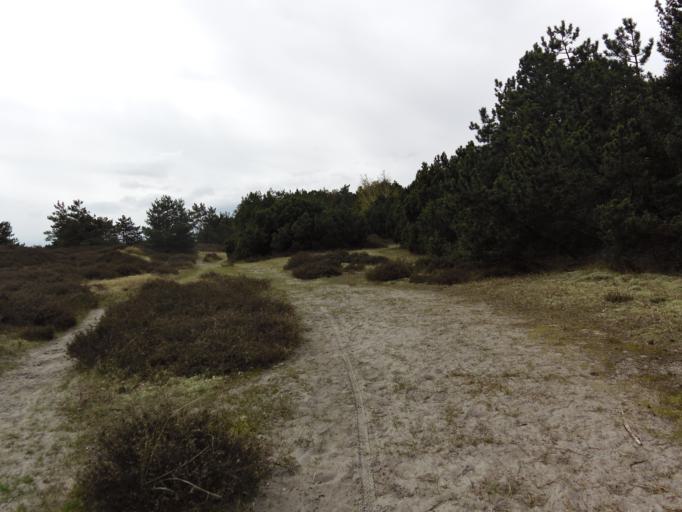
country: DE
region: Mecklenburg-Vorpommern
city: Hiddensee
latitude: 54.5415
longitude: 13.0914
